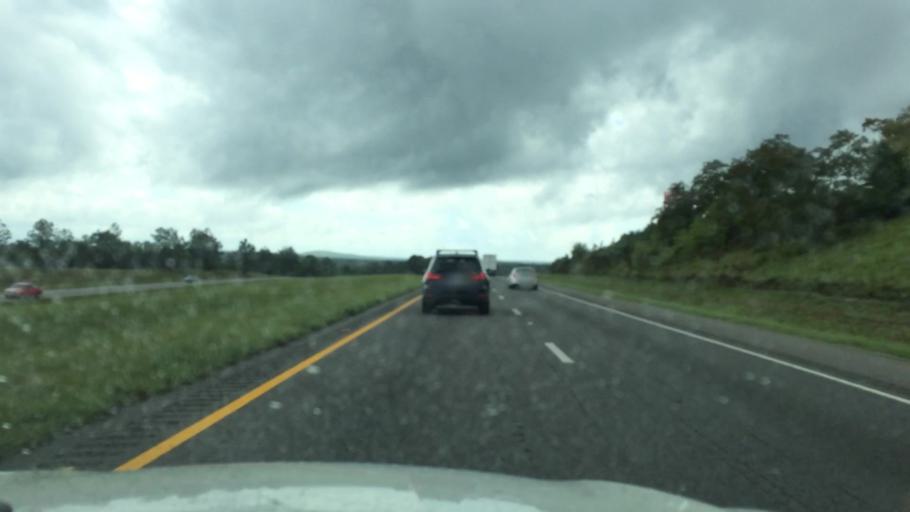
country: US
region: South Carolina
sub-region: Kershaw County
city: Elgin
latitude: 34.1603
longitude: -80.7261
